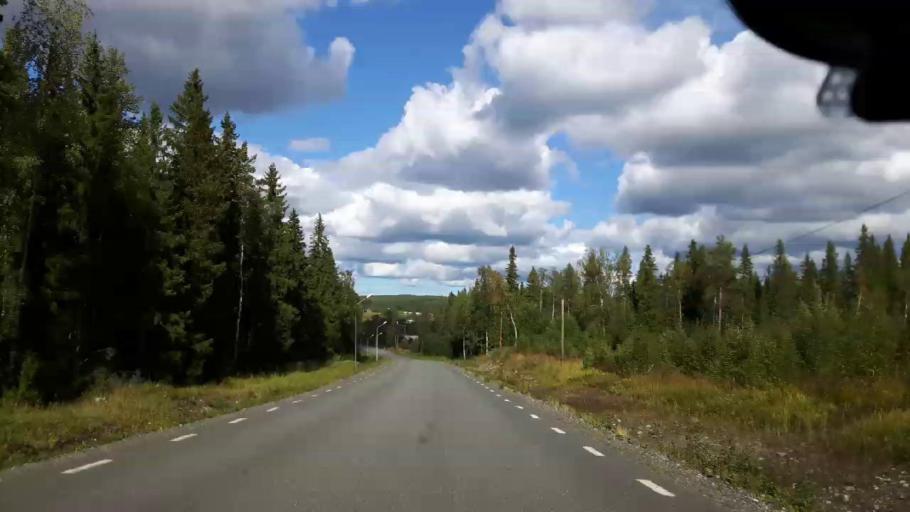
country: SE
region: Jaemtland
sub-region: Braecke Kommun
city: Braecke
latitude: 63.2885
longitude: 15.5881
